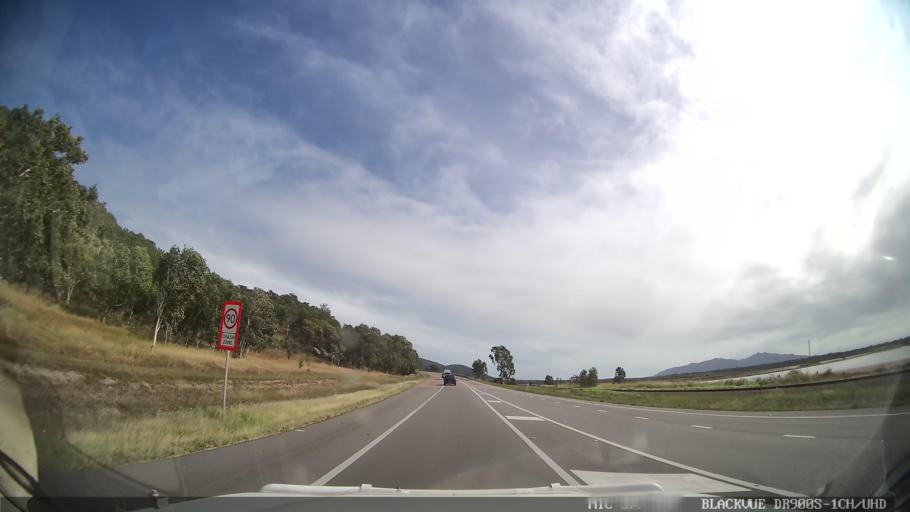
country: AU
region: Queensland
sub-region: Townsville
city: Townsville
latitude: -19.3959
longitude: 147.0211
